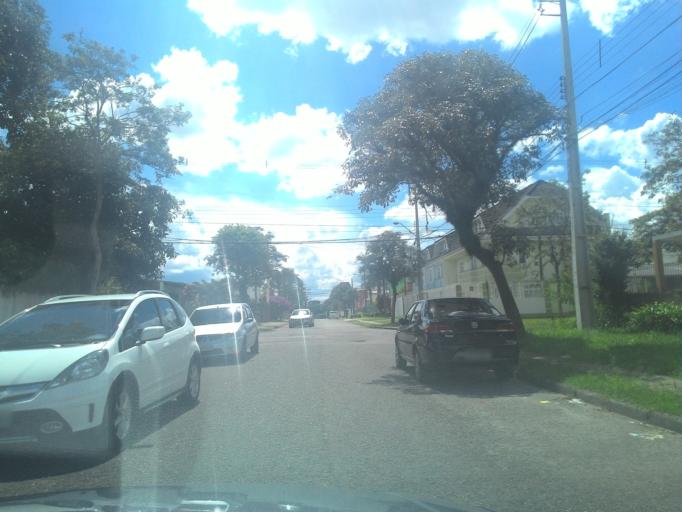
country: BR
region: Parana
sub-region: Pinhais
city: Pinhais
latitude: -25.4541
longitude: -49.2289
